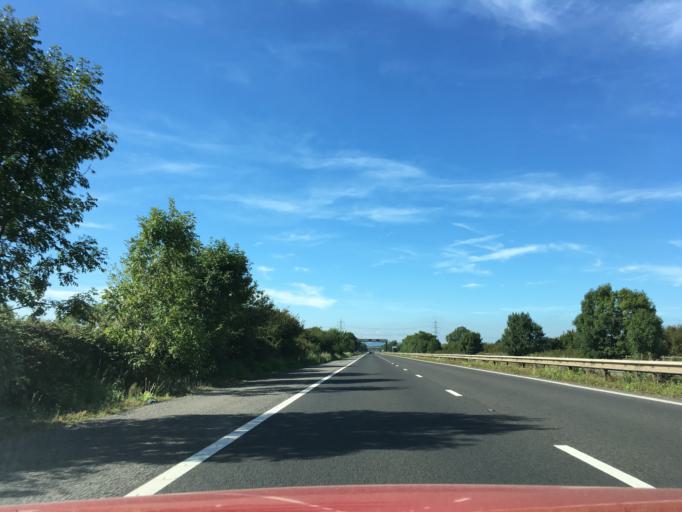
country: GB
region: England
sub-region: South Gloucestershire
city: Almondsbury
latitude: 51.5780
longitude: -2.5888
